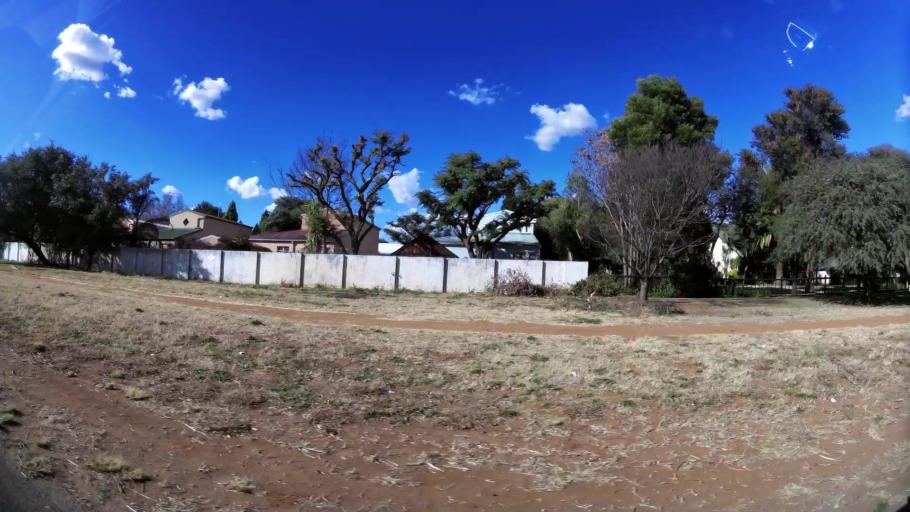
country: ZA
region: North-West
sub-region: Dr Kenneth Kaunda District Municipality
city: Klerksdorp
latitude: -26.8277
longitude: 26.6674
